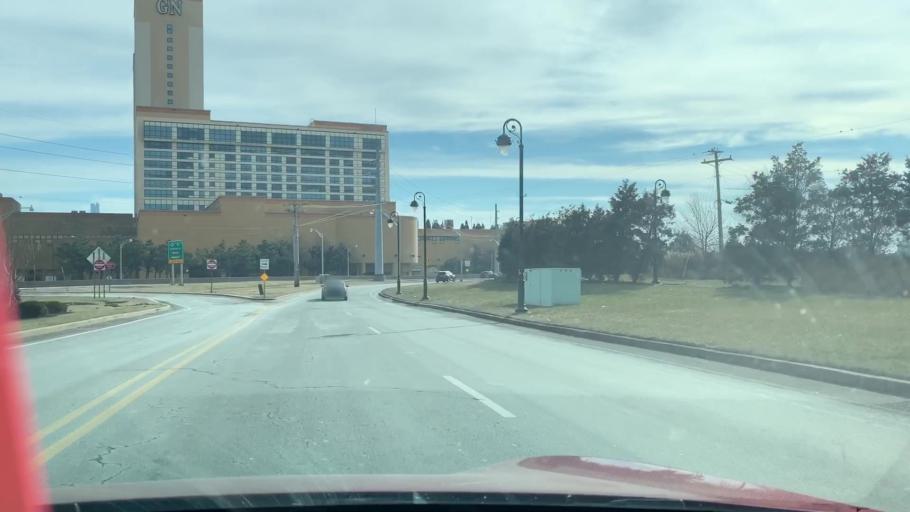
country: US
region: New Jersey
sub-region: Atlantic County
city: Atlantic City
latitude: 39.3821
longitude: -74.4292
